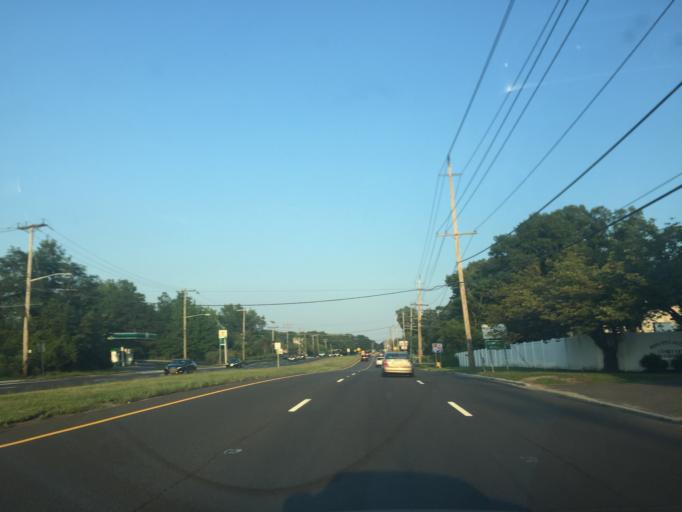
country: US
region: New Jersey
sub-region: Monmouth County
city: Wanamassa
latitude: 40.2281
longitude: -74.0482
